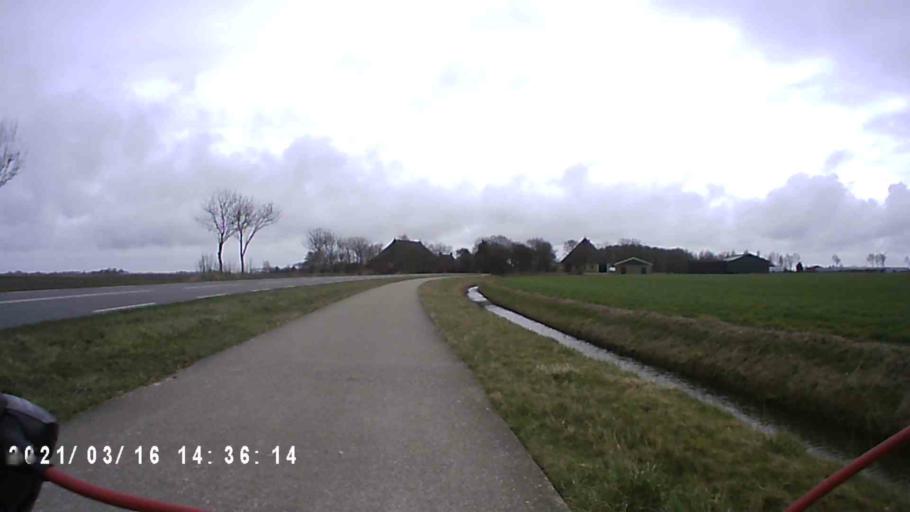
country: NL
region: Friesland
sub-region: Gemeente Harlingen
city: Harlingen
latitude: 53.1460
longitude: 5.4198
